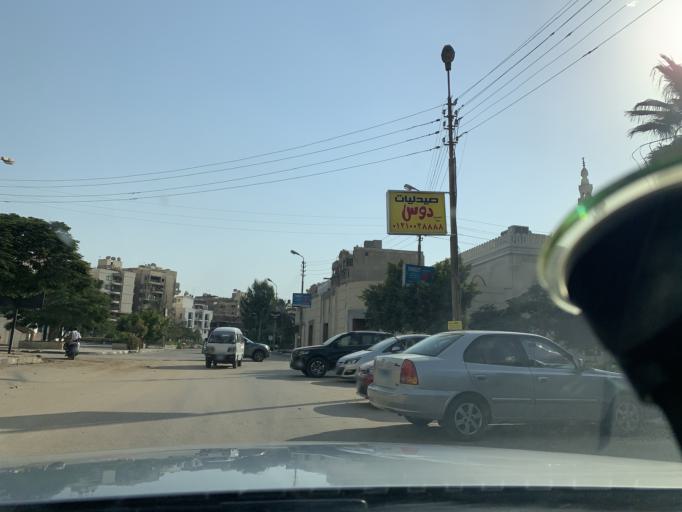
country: EG
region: Muhafazat al Qalyubiyah
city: Al Khankah
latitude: 30.1008
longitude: 31.3763
